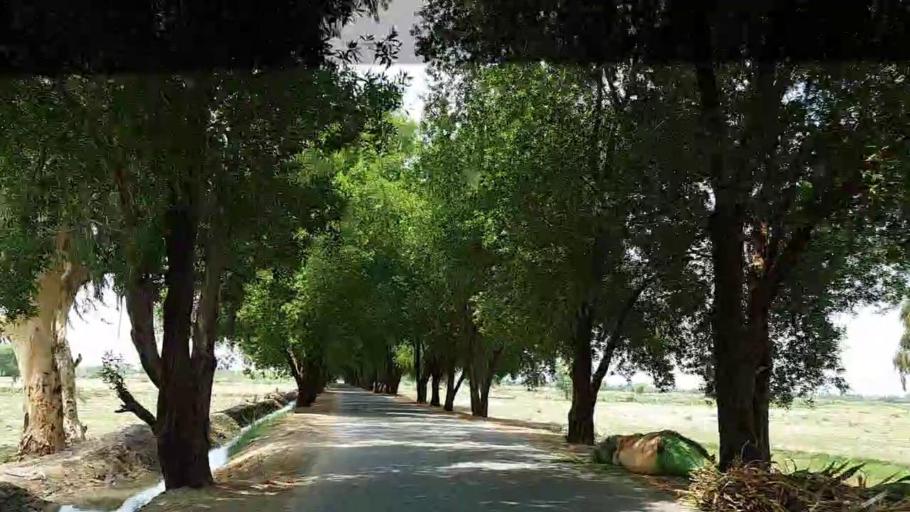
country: PK
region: Sindh
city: Adilpur
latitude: 27.8754
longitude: 69.2757
